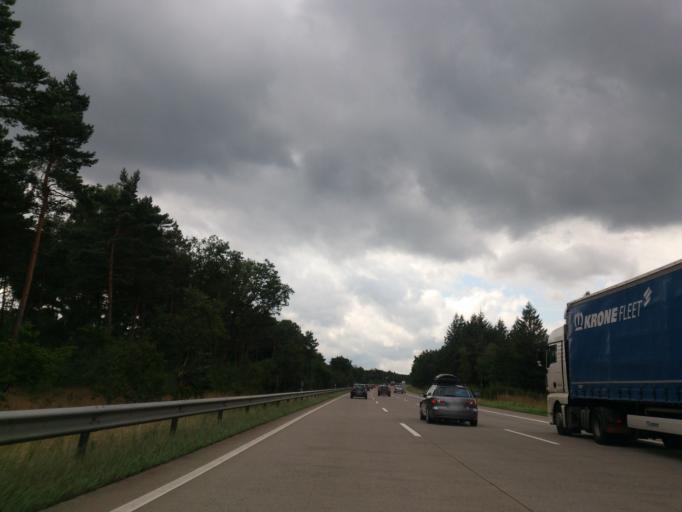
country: DE
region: Lower Saxony
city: Bispingen
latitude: 53.0385
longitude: 9.9485
